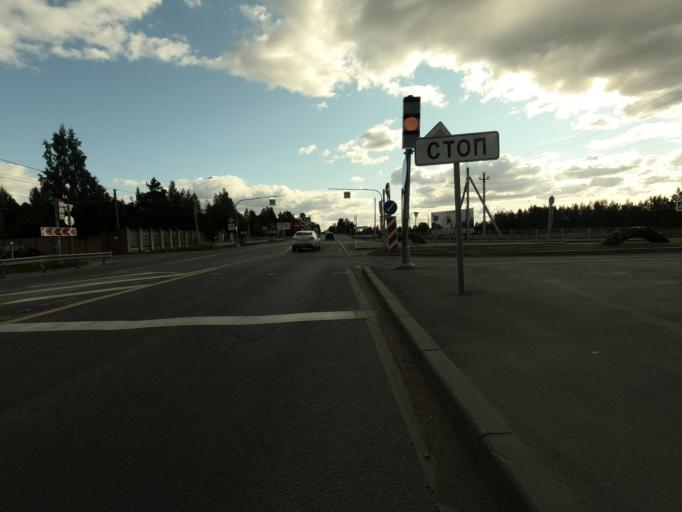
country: RU
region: Leningrad
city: Vsevolozhsk
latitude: 59.9866
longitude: 30.6560
